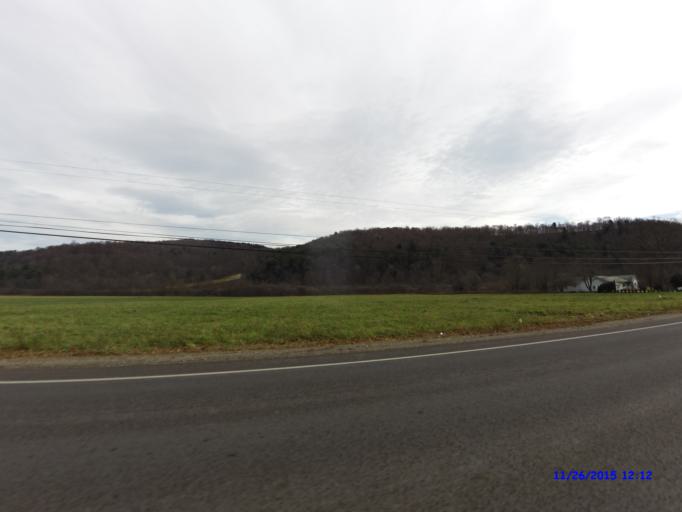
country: US
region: New York
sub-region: Cattaraugus County
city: Allegany
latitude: 42.1640
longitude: -78.5061
